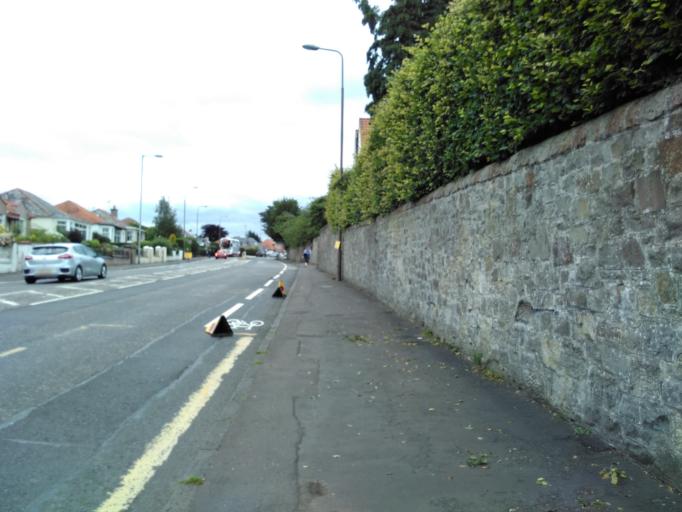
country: GB
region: Scotland
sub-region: Midlothian
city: Loanhead
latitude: 55.9122
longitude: -3.1443
